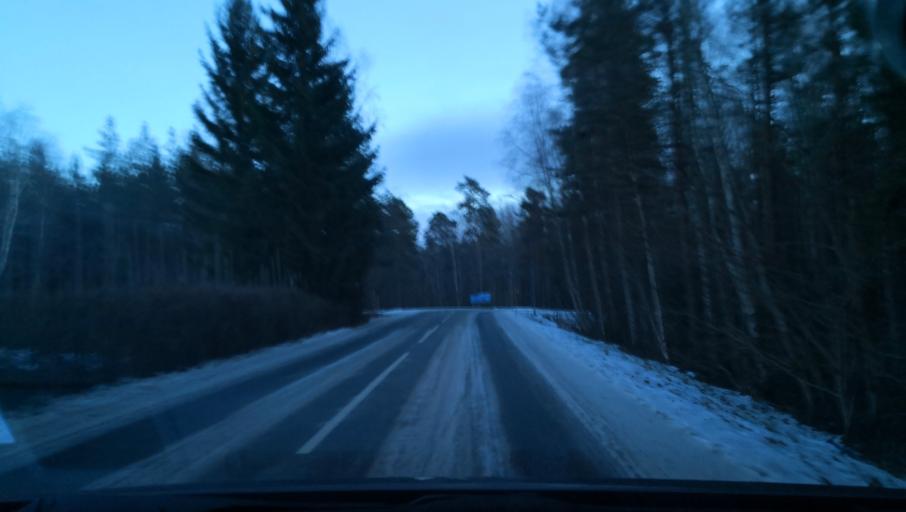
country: SE
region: Soedermanland
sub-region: Katrineholms Kommun
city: Katrineholm
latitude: 59.0838
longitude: 16.2213
